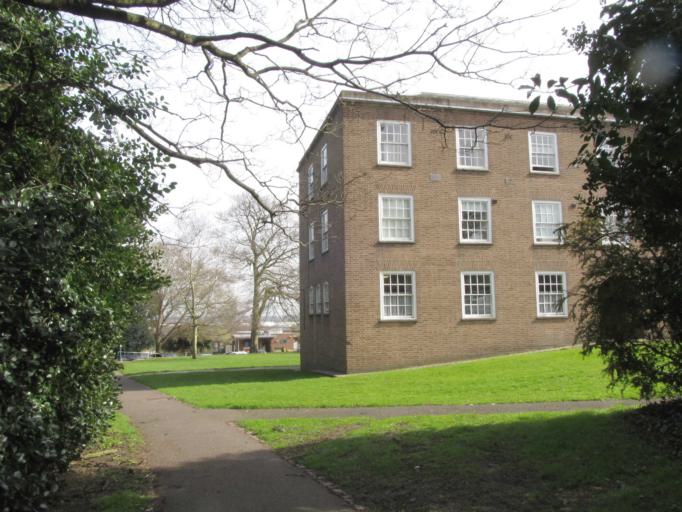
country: GB
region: England
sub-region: Nottingham
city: Nottingham
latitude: 52.9428
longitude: -1.1954
